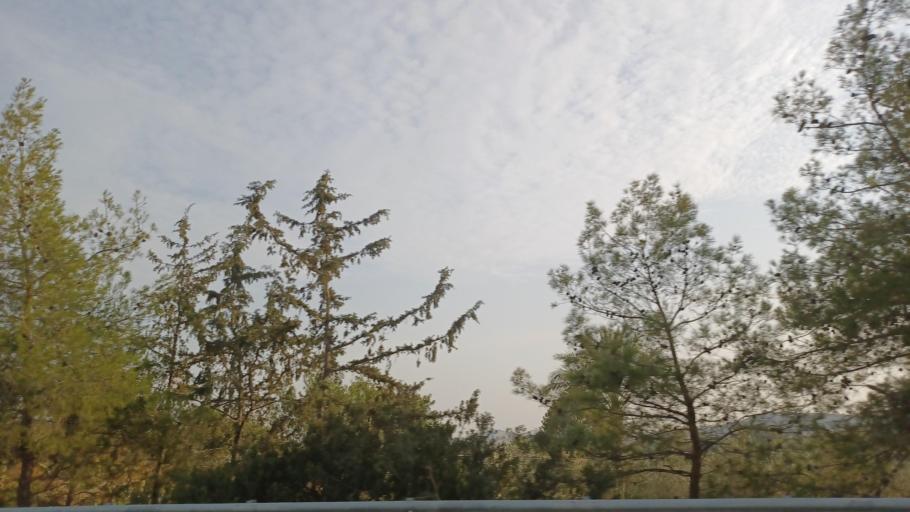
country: CY
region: Larnaka
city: Tersefanou
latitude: 34.8595
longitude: 33.4682
